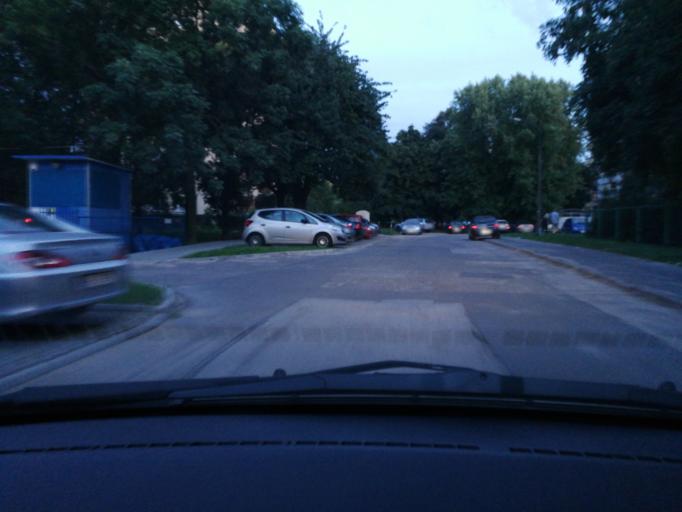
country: PL
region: Masovian Voivodeship
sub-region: Warszawa
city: Targowek
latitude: 52.2919
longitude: 21.0228
